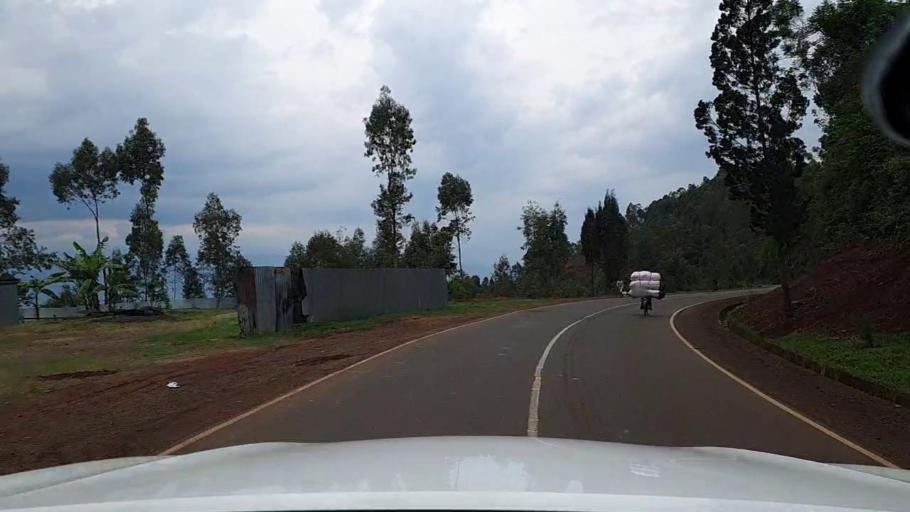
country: RW
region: Western Province
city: Cyangugu
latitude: -2.6458
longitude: 28.9629
